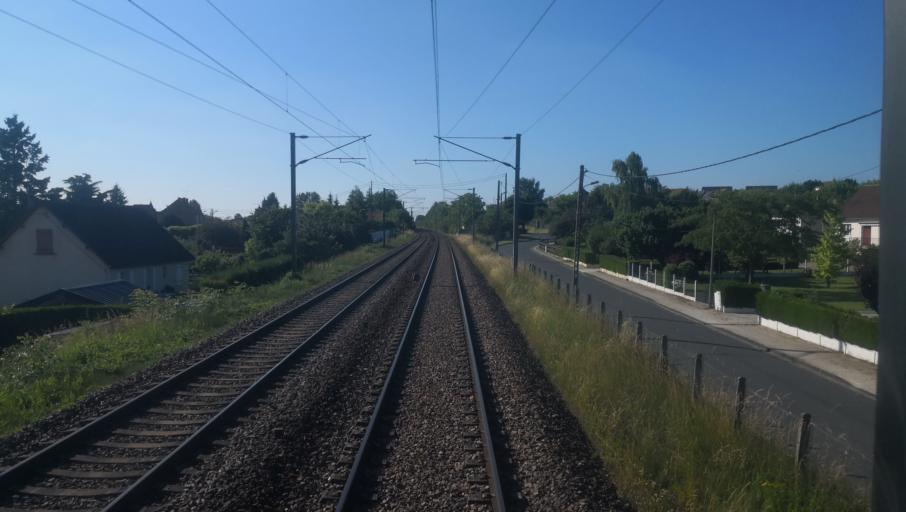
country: FR
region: Centre
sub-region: Departement du Loiret
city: Bonny-sur-Loire
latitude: 47.5526
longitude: 2.8498
